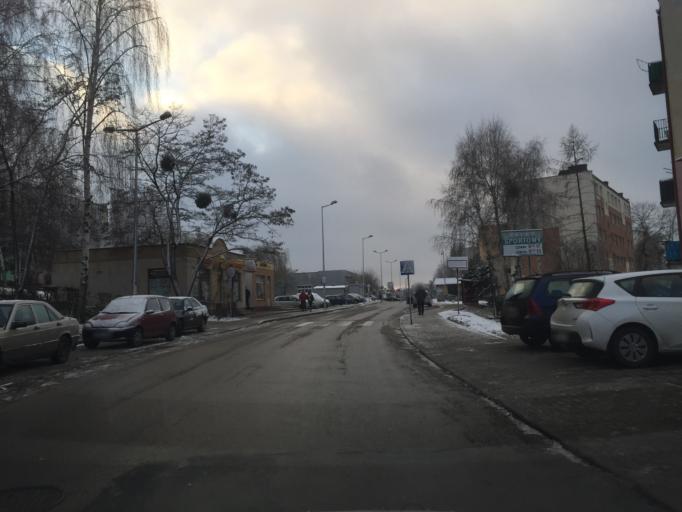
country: PL
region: Kujawsko-Pomorskie
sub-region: Powiat brodnicki
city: Brodnica
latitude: 53.2490
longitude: 19.4095
